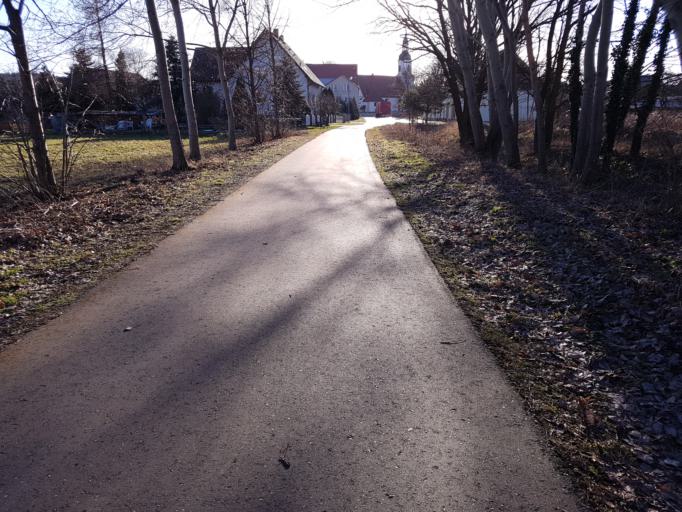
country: DE
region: Brandenburg
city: Groden
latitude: 51.4096
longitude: 13.5725
